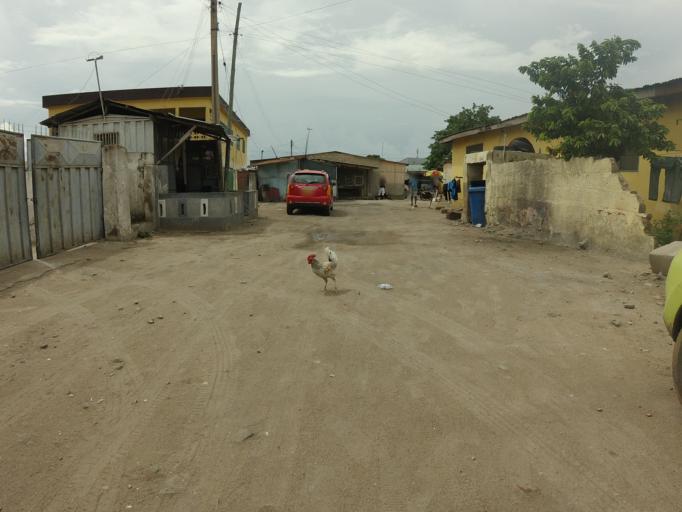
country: GH
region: Greater Accra
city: Accra
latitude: 5.5981
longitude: -0.2197
